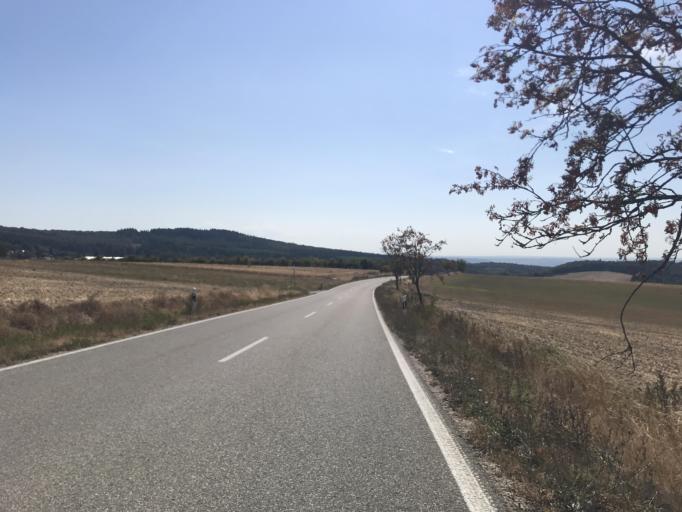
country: DE
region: Hesse
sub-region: Regierungsbezirk Darmstadt
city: Rudesheim am Rhein
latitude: 50.0413
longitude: 7.9369
